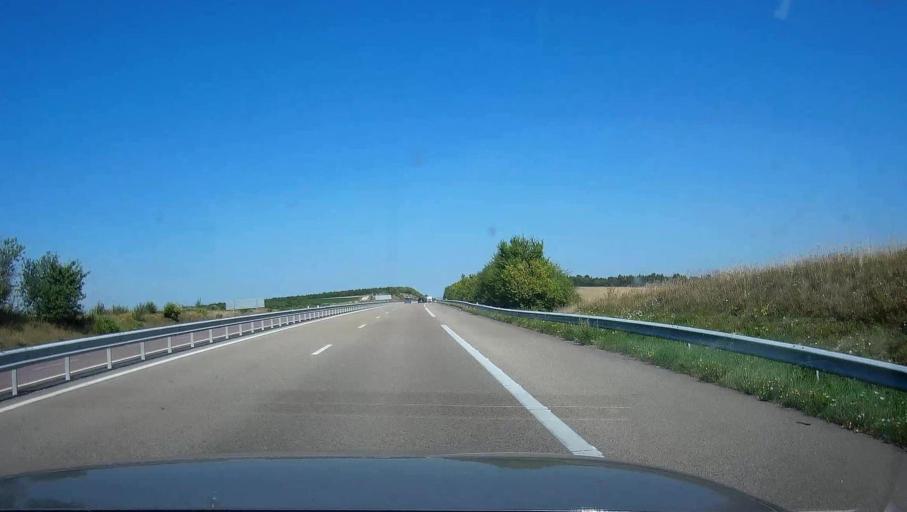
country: FR
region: Champagne-Ardenne
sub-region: Departement de l'Aube
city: Creney-pres-Troyes
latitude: 48.3696
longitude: 4.1588
